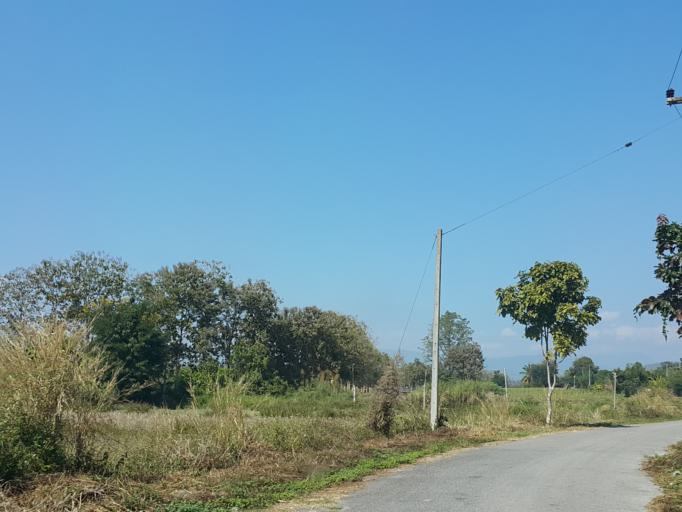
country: TH
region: Chiang Mai
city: Mae Taeng
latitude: 19.0349
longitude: 98.9813
